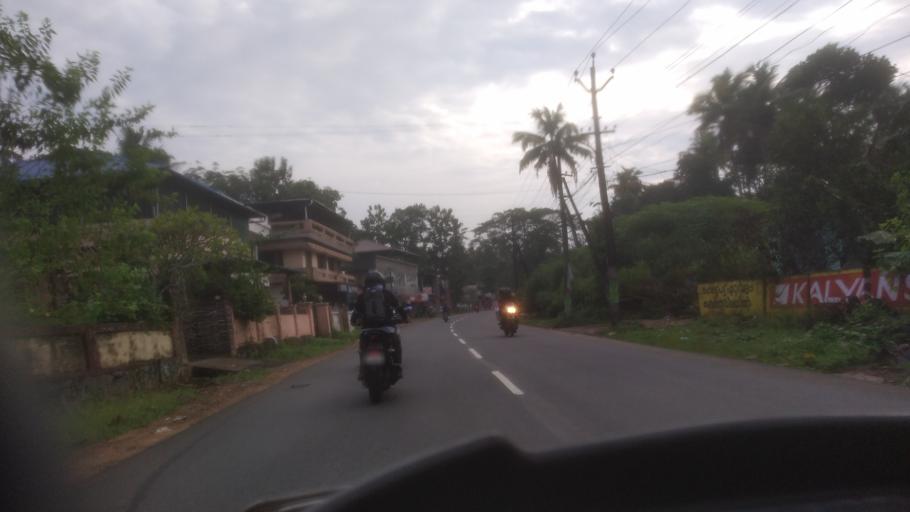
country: IN
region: Kerala
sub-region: Ernakulam
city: Kotamangalam
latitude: 10.0589
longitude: 76.6490
